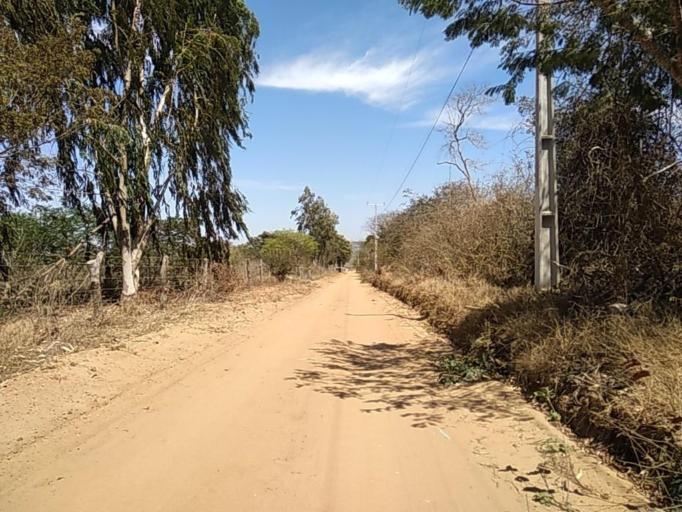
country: BR
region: Bahia
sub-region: Caetite
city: Caetite
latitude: -13.9768
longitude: -42.5154
